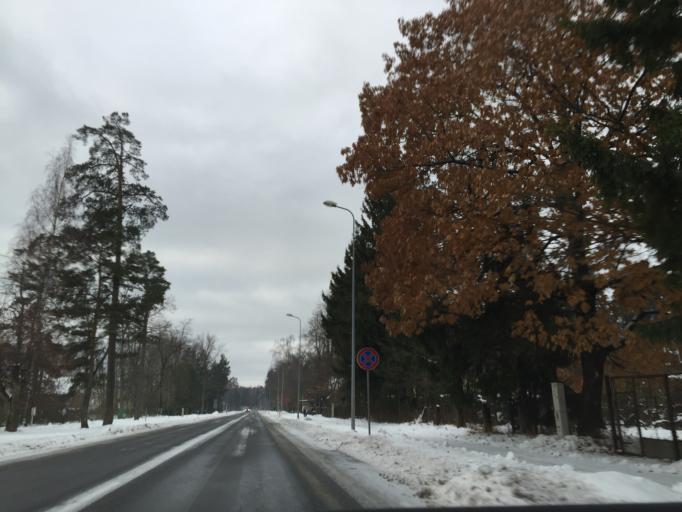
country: LV
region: Saulkrastu
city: Saulkrasti
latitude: 57.2407
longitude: 24.3993
